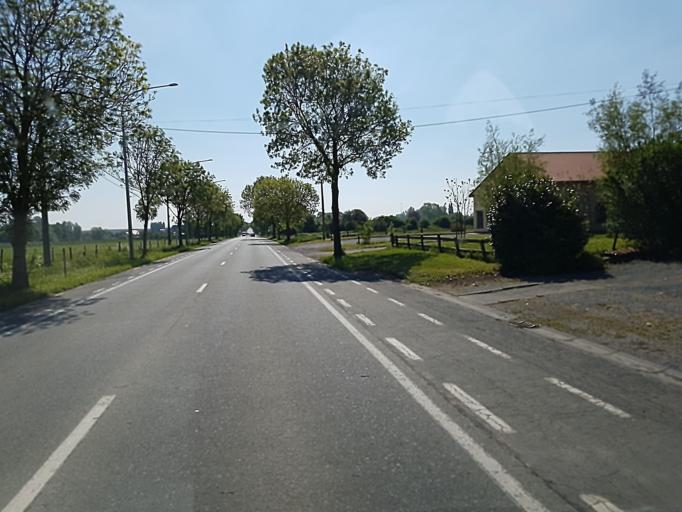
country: BE
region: Wallonia
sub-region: Province du Hainaut
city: Brugelette
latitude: 50.5896
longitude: 3.8406
